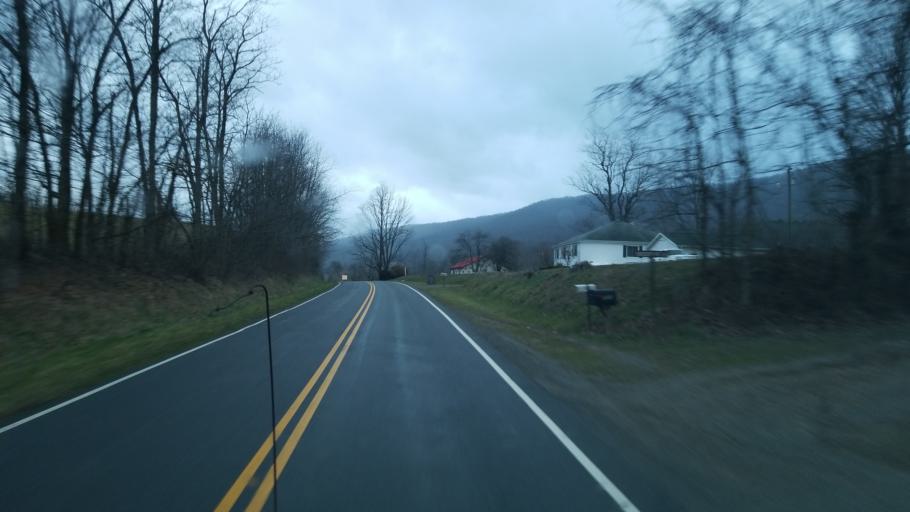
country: US
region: Virginia
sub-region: Giles County
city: Narrows
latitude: 37.2050
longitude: -80.8144
